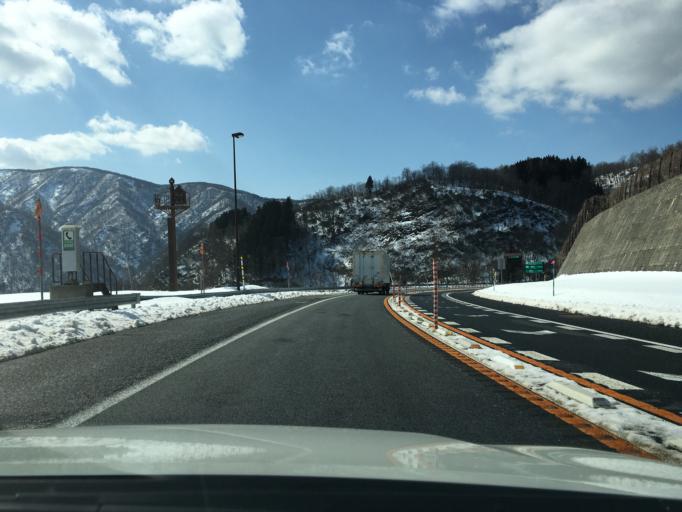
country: JP
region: Yamagata
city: Tsuruoka
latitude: 38.5722
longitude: 139.9137
